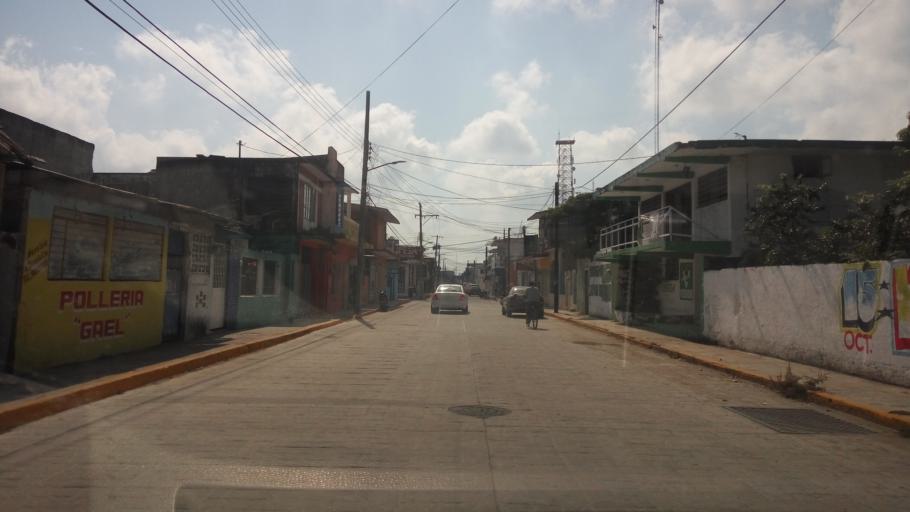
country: MX
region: Tabasco
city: Frontera
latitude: 18.5335
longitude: -92.6486
